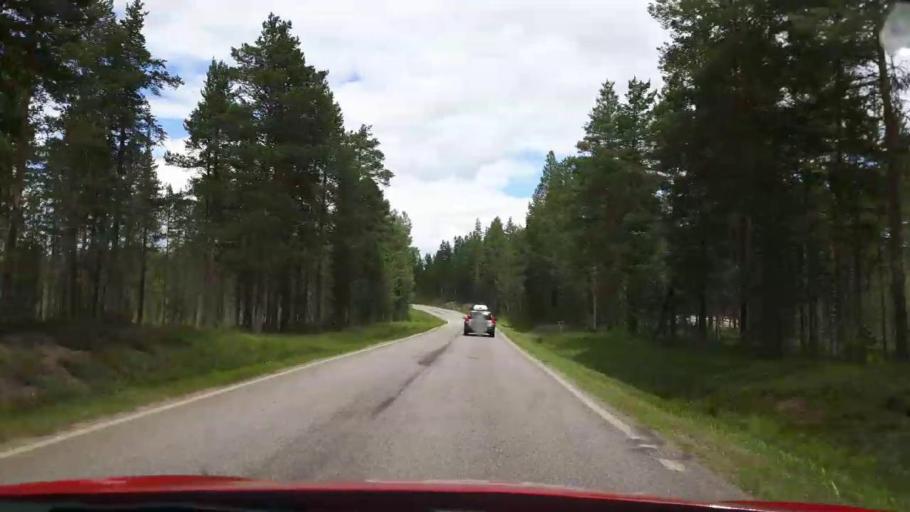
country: NO
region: Hedmark
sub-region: Trysil
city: Innbygda
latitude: 61.8354
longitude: 12.9567
